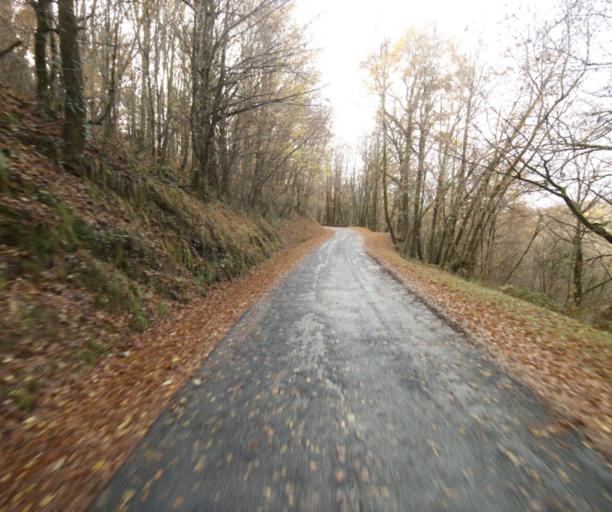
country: FR
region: Limousin
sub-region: Departement de la Correze
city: Sainte-Fereole
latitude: 45.2088
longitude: 1.6327
